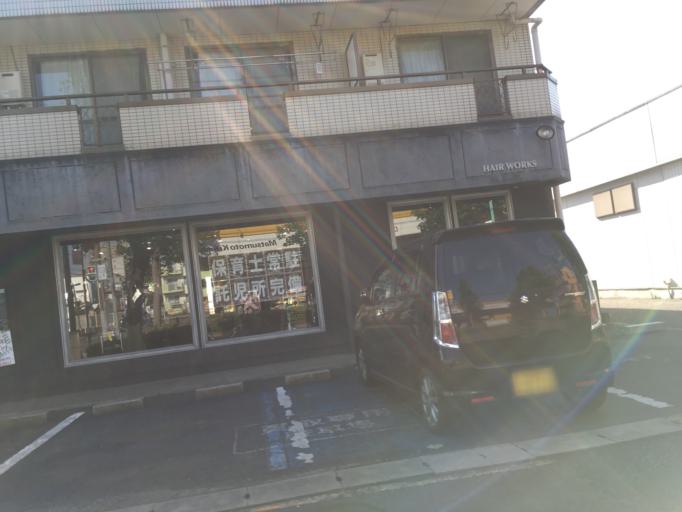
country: JP
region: Chiba
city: Nagareyama
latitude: 35.8200
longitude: 139.9141
